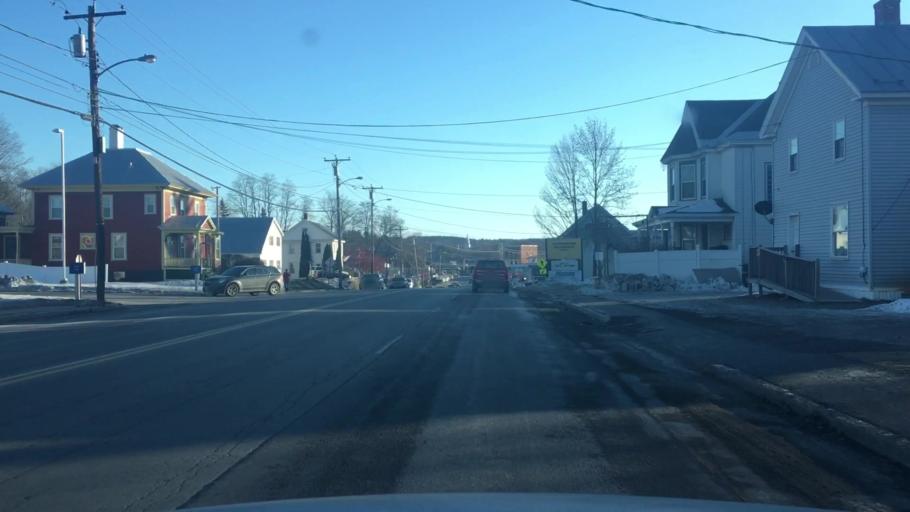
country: US
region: Maine
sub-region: Somerset County
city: Skowhegan
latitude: 44.7693
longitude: -69.7214
